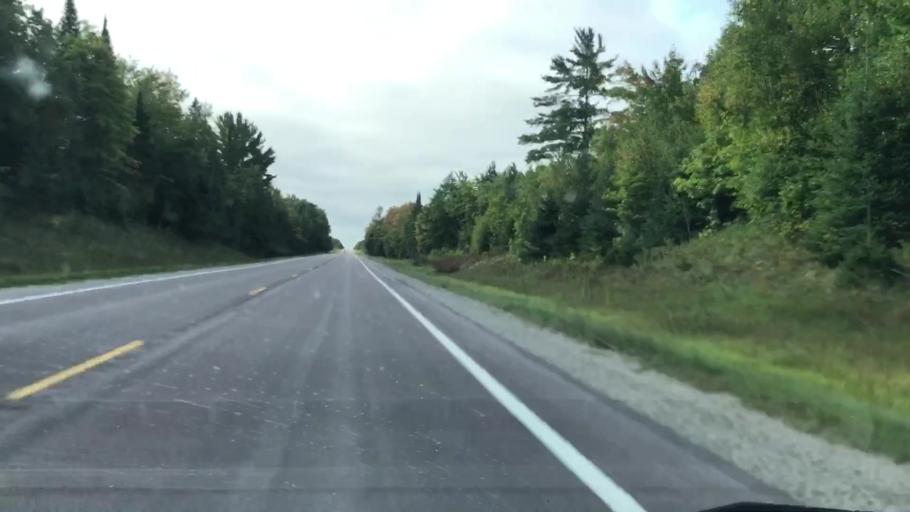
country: US
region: Michigan
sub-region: Luce County
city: Newberry
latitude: 46.2941
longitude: -85.5694
